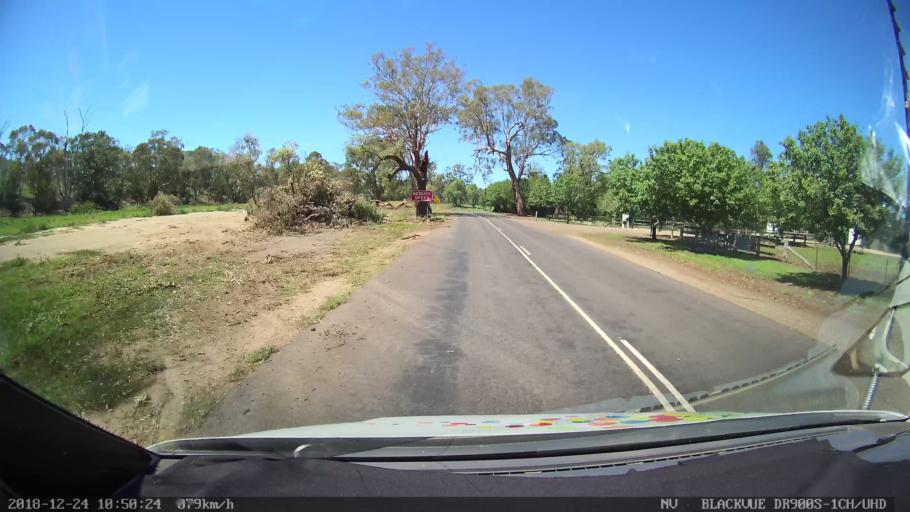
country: AU
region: New South Wales
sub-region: Upper Hunter Shire
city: Merriwa
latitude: -31.9597
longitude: 150.4240
